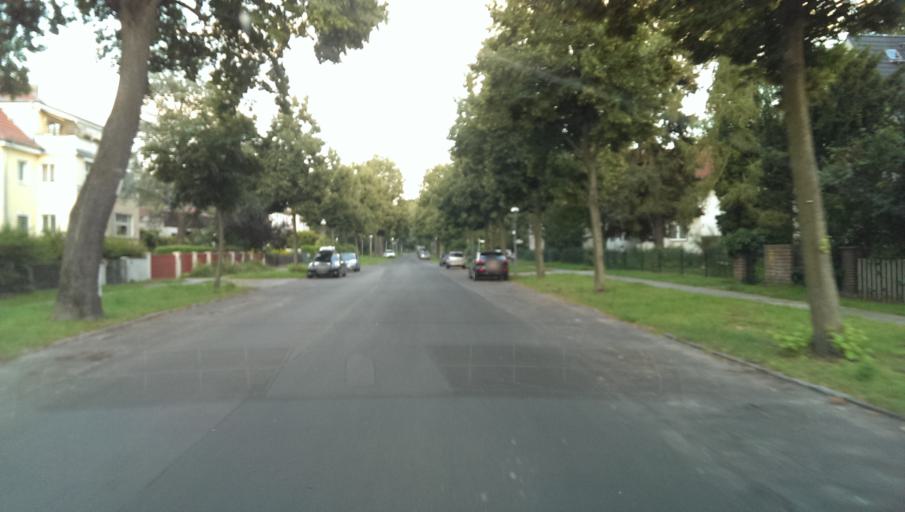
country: DE
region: Berlin
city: Lichterfelde
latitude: 52.4173
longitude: 13.3078
